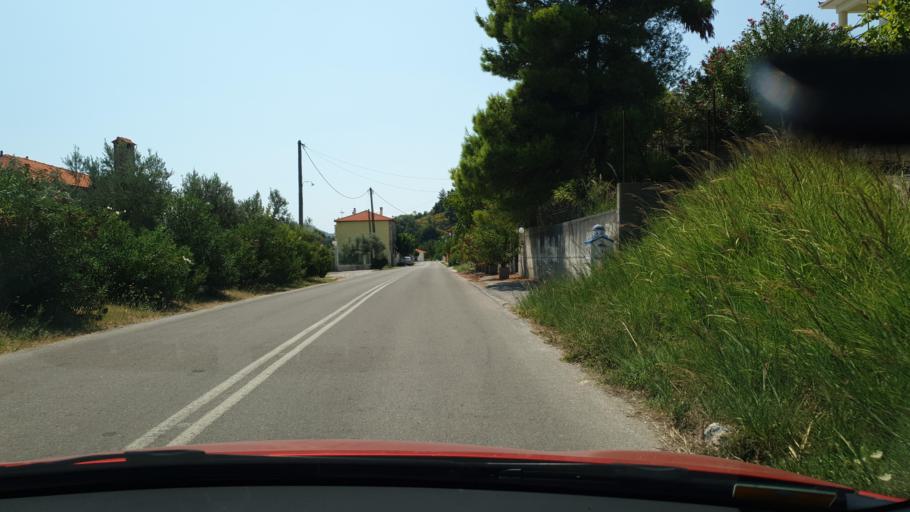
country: GR
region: Central Greece
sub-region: Nomos Evvoias
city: Kymi
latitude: 38.6158
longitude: 24.0792
